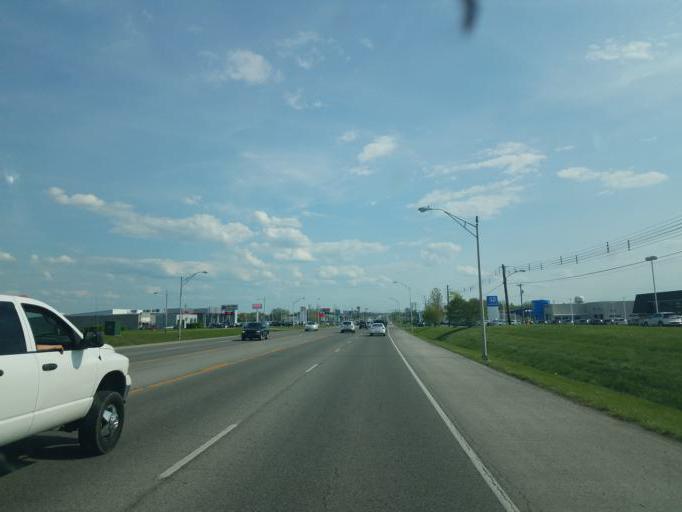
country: US
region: Kentucky
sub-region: Warren County
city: Bowling Green
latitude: 36.9571
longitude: -86.4281
